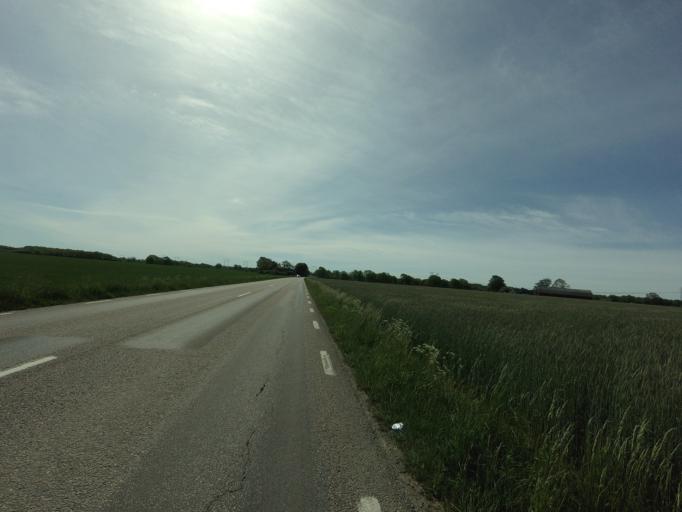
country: SE
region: Skane
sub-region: Helsingborg
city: Odakra
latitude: 56.1424
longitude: 12.6847
